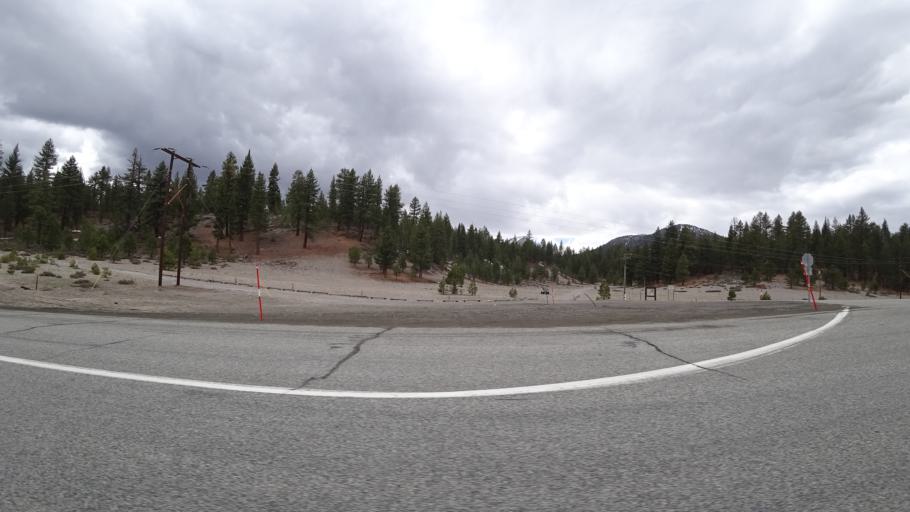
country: US
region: California
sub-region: Mono County
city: Mammoth Lakes
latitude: 37.7640
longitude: -118.9993
